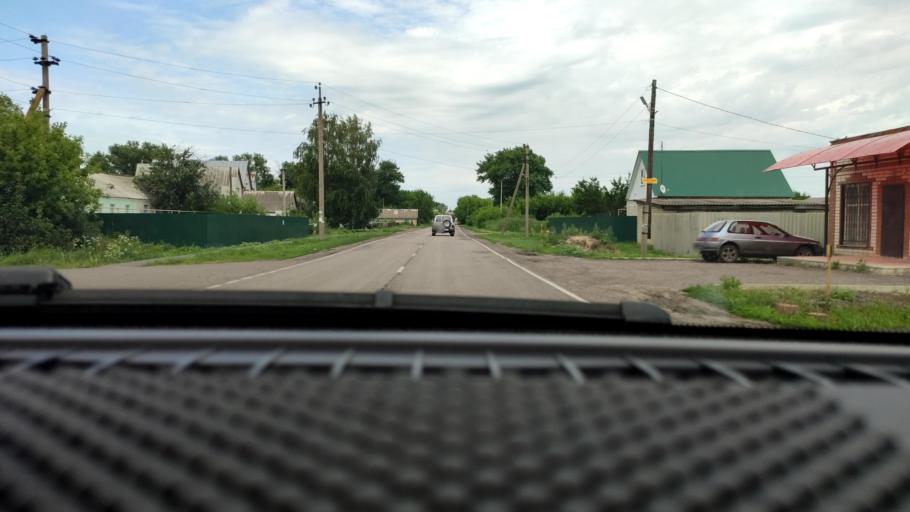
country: RU
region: Voronezj
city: Panino
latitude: 51.6552
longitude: 40.1205
